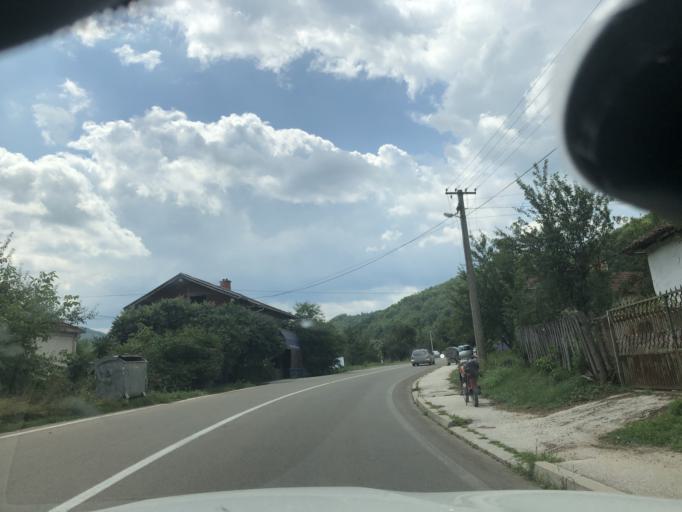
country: RS
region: Central Serbia
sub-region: Jablanicki Okrug
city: Medvega
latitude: 42.8316
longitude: 21.5847
